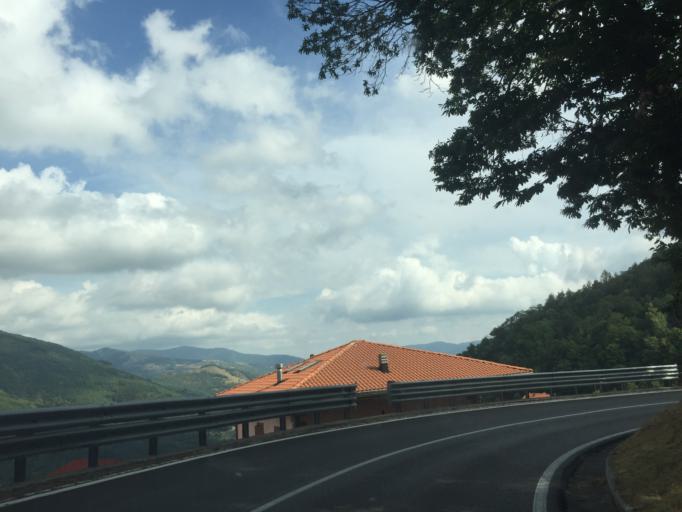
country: IT
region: Tuscany
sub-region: Provincia di Pistoia
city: Cutigliano
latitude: 44.1218
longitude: 10.7266
